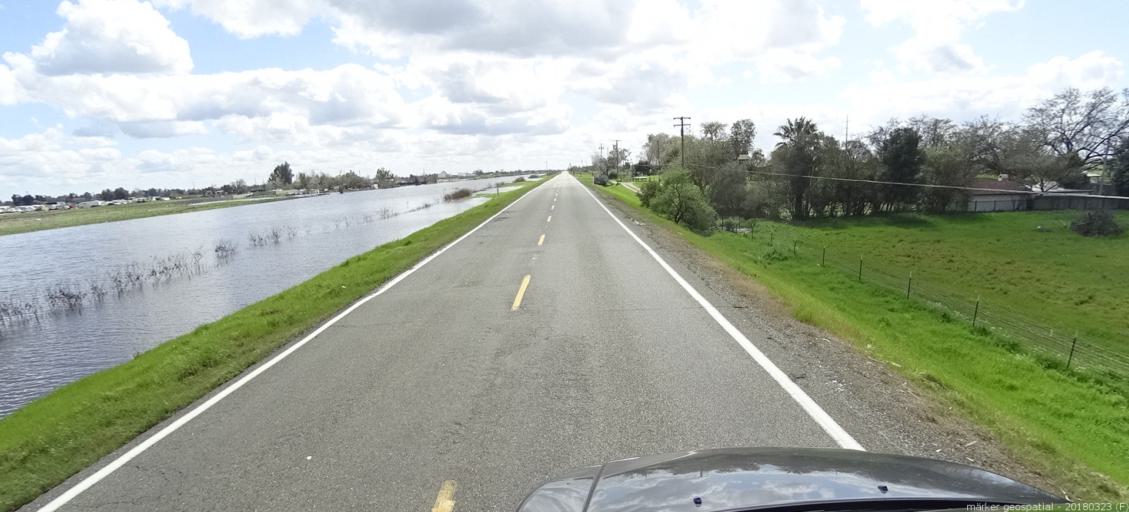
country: US
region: California
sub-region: Sacramento County
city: Elverta
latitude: 38.7042
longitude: -121.4857
